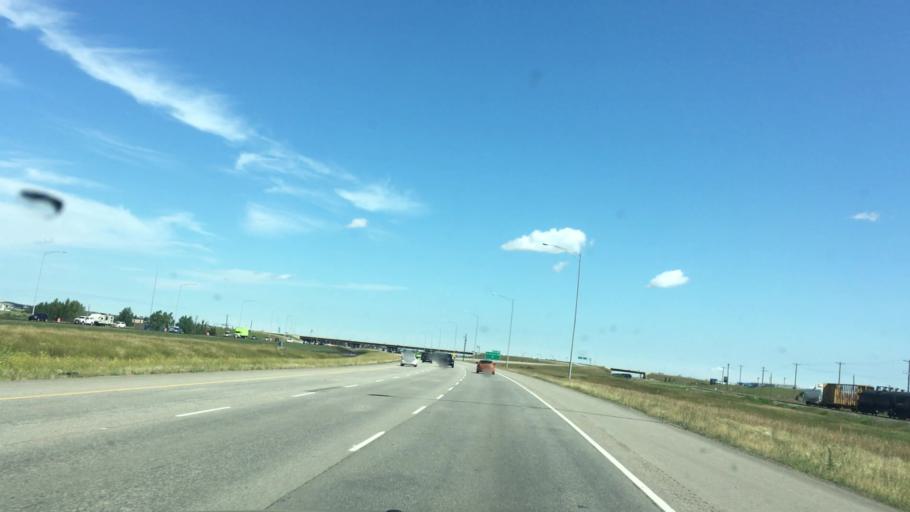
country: CA
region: Alberta
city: Beaumont
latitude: 53.3855
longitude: -113.5156
